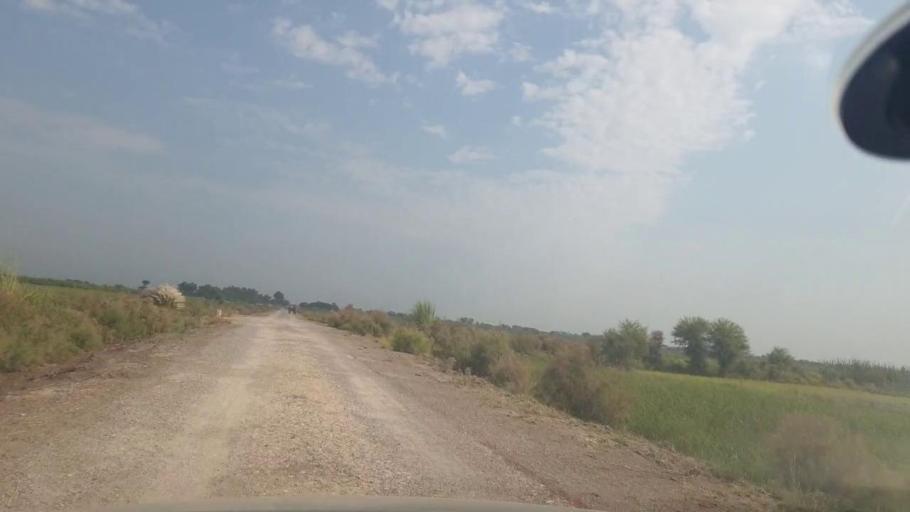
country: PK
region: Balochistan
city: Mehrabpur
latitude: 28.0455
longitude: 68.1221
